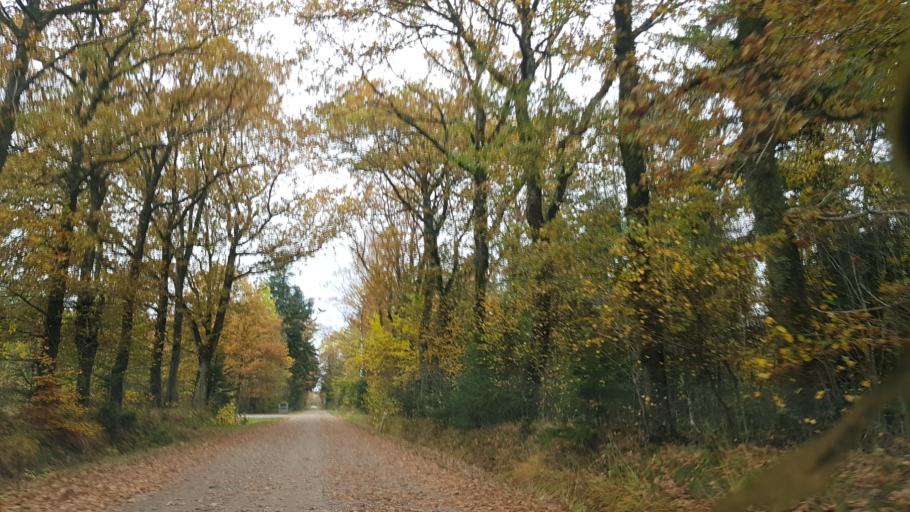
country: DK
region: South Denmark
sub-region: Tonder Kommune
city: Sherrebek
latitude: 55.1847
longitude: 8.7645
